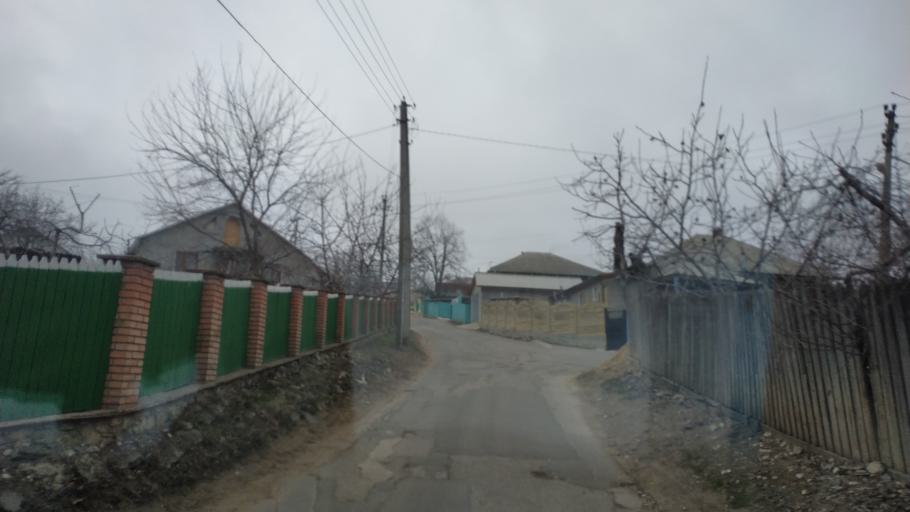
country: MD
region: Hincesti
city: Hincesti
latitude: 46.9073
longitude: 28.6684
